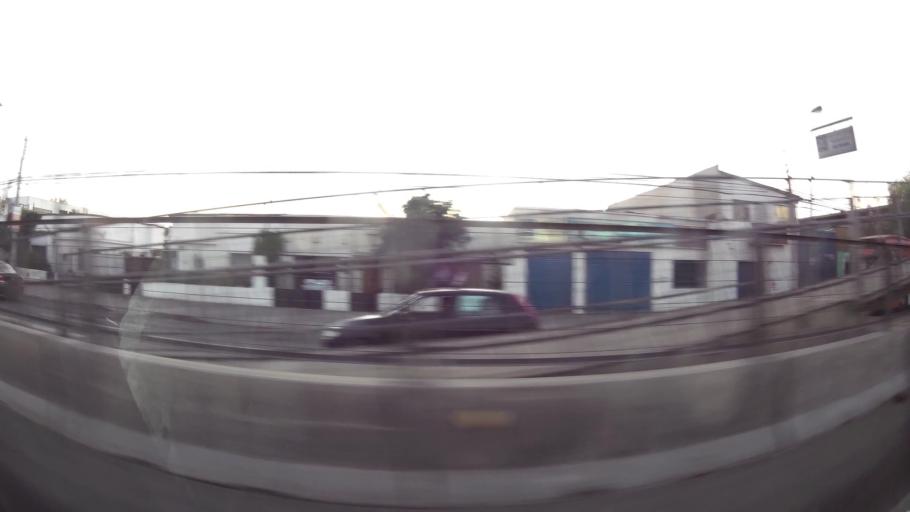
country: CL
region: Santiago Metropolitan
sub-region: Provincia de Santiago
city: Lo Prado
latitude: -33.4473
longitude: -70.6924
